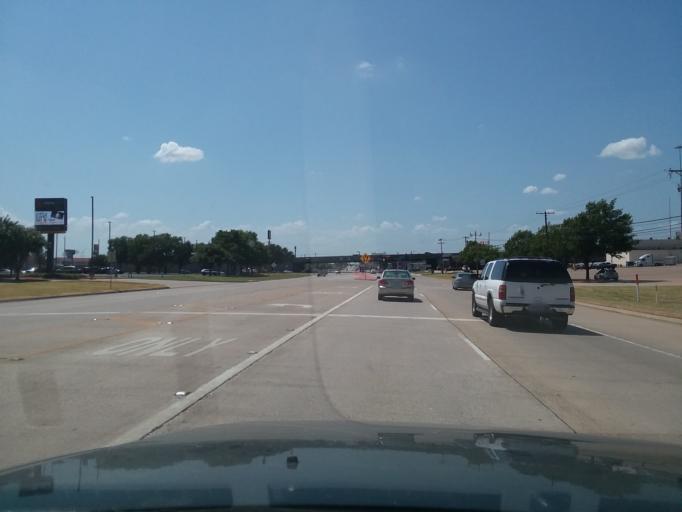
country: US
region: Texas
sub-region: Tarrant County
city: Euless
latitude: 32.8405
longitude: -97.0999
